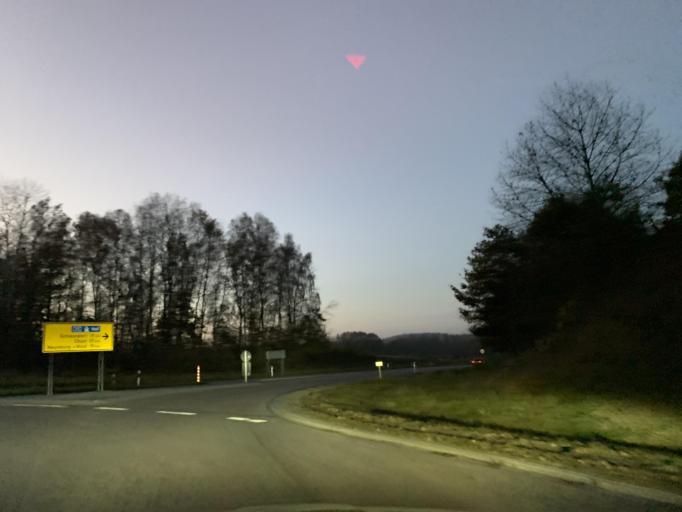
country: DE
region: Bavaria
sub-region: Upper Palatinate
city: Bruck in der Oberpfalz
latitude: 49.2507
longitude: 12.2964
